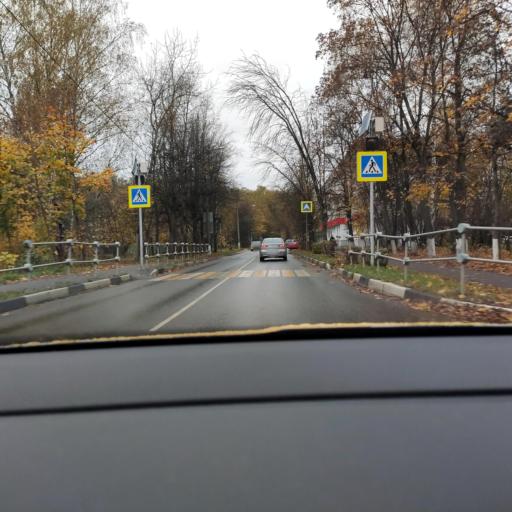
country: RU
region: Moskovskaya
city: Ivanteyevka
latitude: 55.9622
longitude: 37.9156
